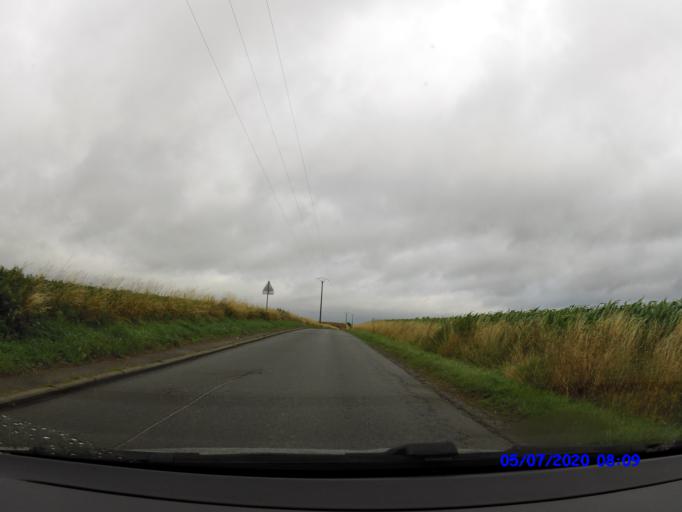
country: BE
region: Wallonia
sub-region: Province du Hainaut
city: Fleurus
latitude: 50.5264
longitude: 4.5546
